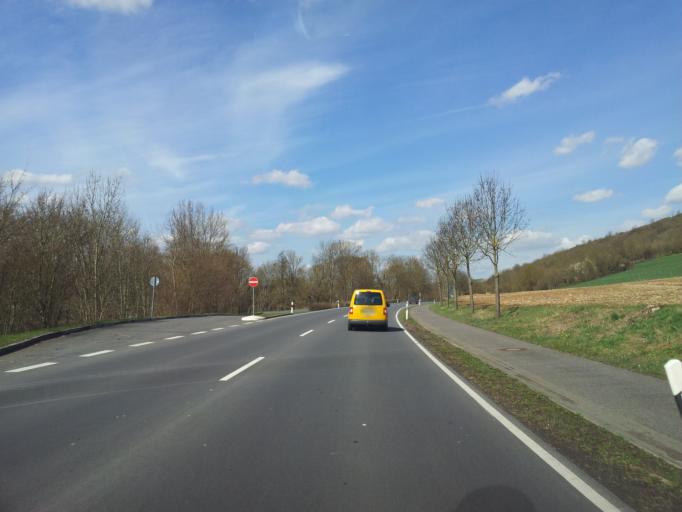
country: DE
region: Baden-Wuerttemberg
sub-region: Regierungsbezirk Stuttgart
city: Lauda-Konigshofen
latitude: 49.5660
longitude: 9.7150
